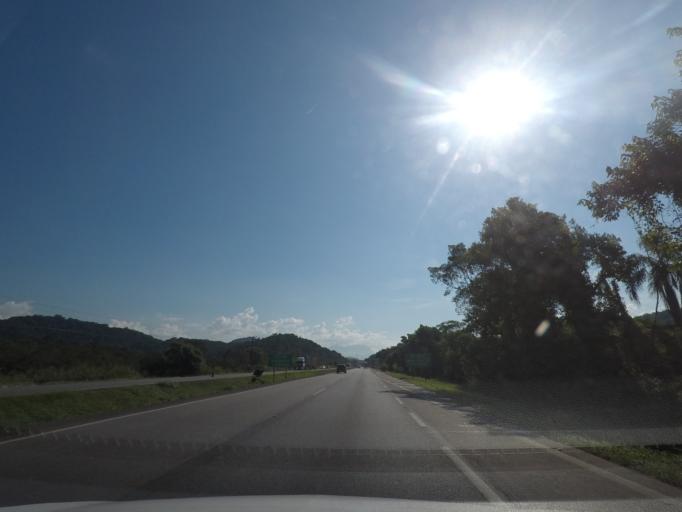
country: BR
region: Parana
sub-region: Antonina
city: Antonina
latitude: -25.5392
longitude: -48.6929
